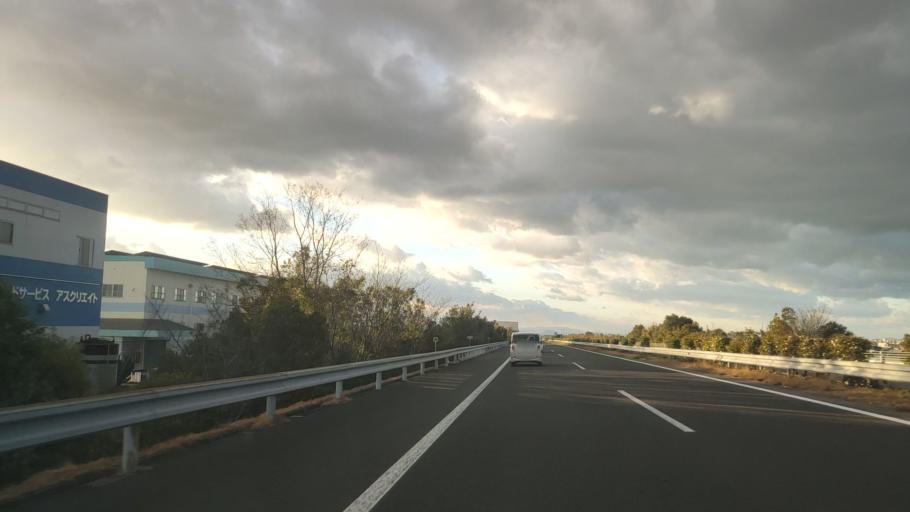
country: JP
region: Ehime
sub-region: Shikoku-chuo Shi
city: Matsuyama
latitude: 33.7854
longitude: 132.8436
